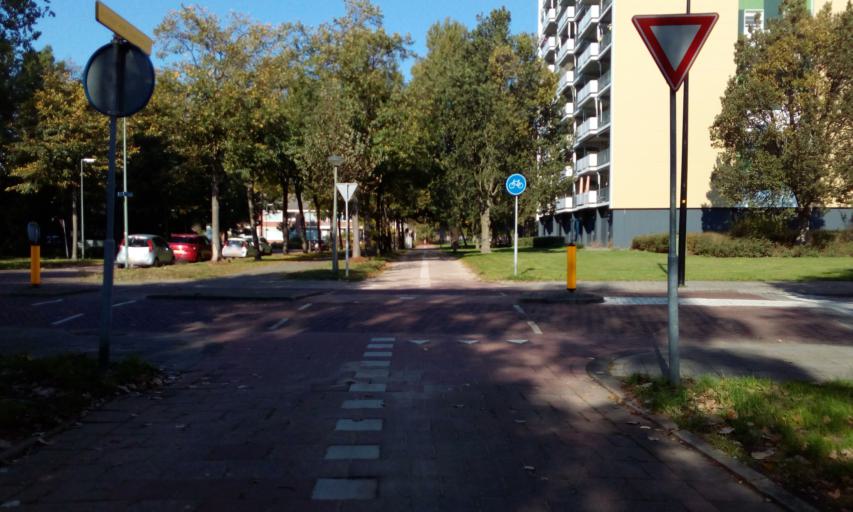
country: NL
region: South Holland
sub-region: Gemeente Vlaardingen
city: Vlaardingen
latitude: 51.9249
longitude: 4.3493
